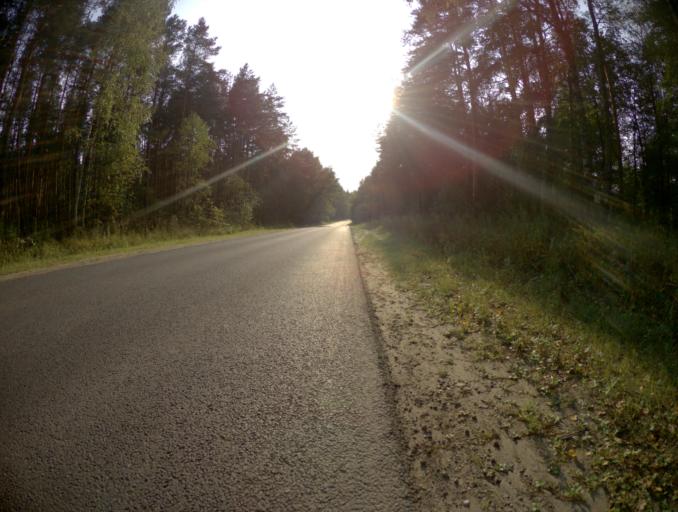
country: RU
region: Vladimir
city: Kommunar
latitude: 56.1257
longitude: 40.4797
